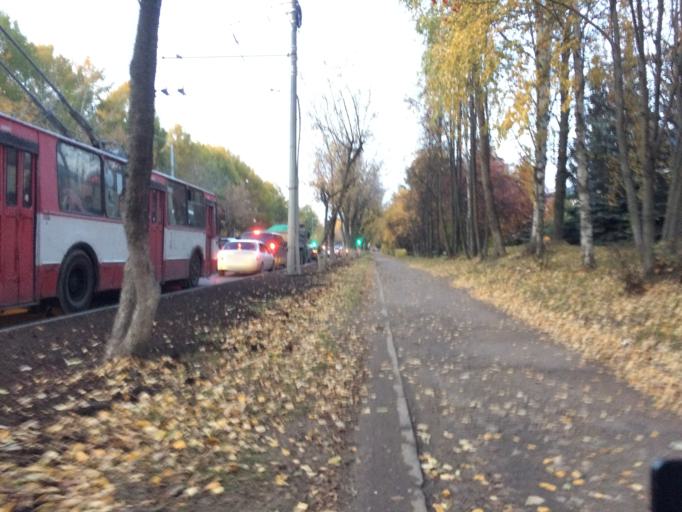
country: RU
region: Mariy-El
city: Yoshkar-Ola
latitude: 56.6120
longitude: 47.8809
